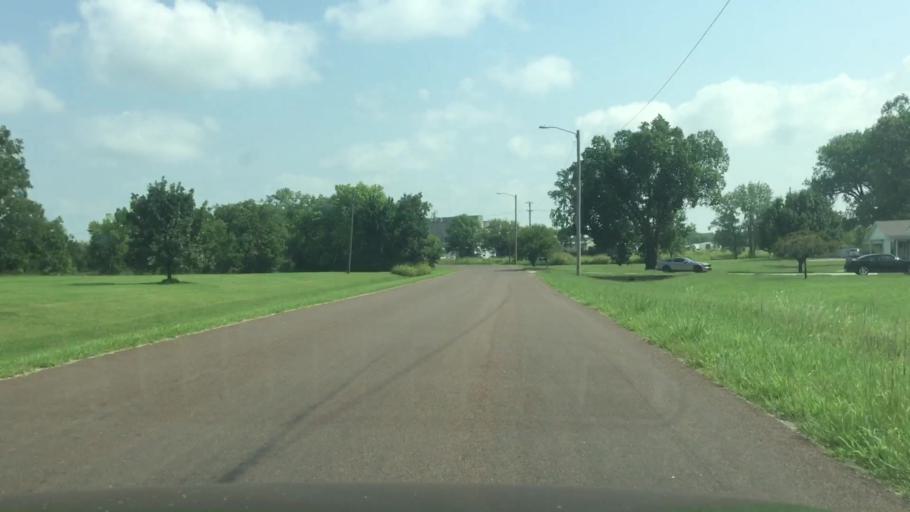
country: US
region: Kansas
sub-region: Allen County
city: Iola
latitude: 37.9047
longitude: -95.4071
